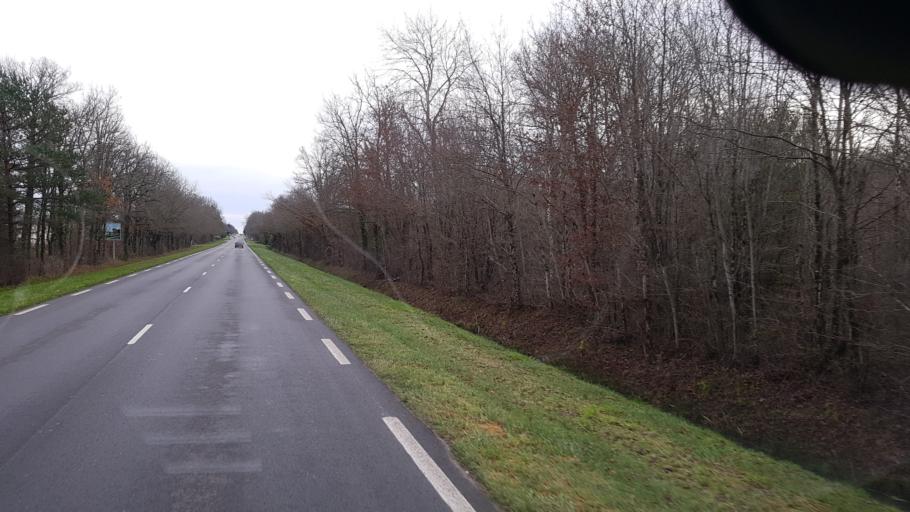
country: FR
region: Centre
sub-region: Departement du Loiret
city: Menestreau-en-Villette
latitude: 47.6579
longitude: 1.9833
